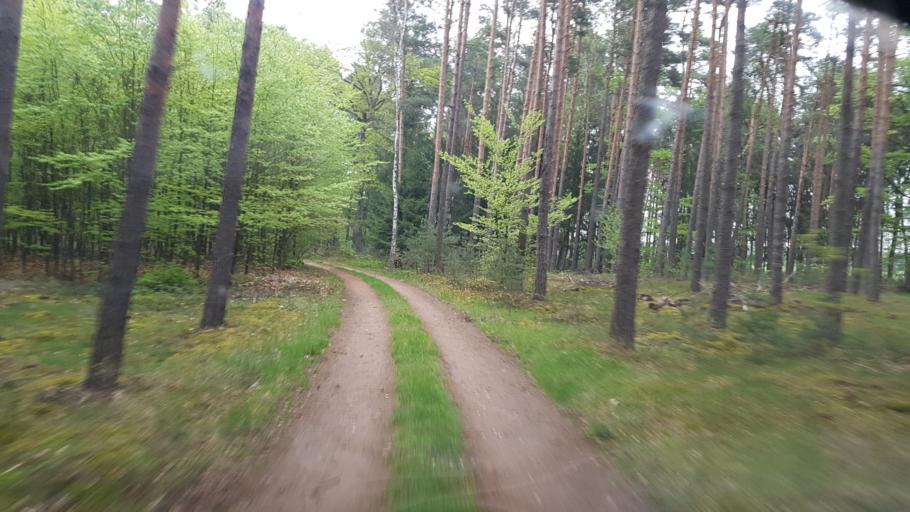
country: DE
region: Brandenburg
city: Schonewalde
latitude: 51.7078
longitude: 13.5262
